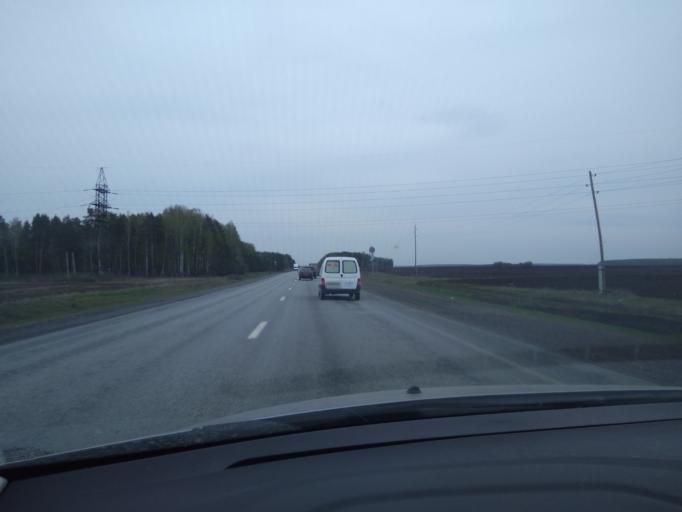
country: RU
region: Sverdlovsk
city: Gryaznovskoye
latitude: 56.7815
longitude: 61.6153
